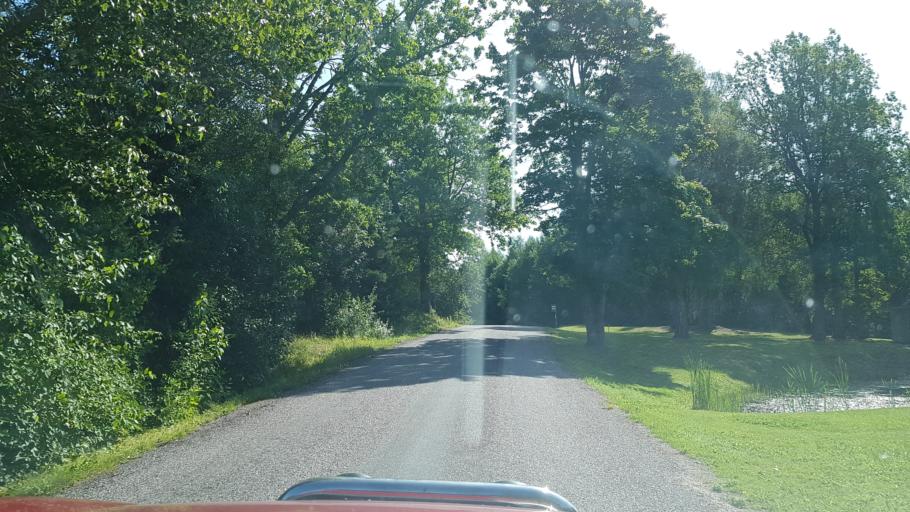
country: EE
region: Vorumaa
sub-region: Voru linn
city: Voru
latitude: 57.7084
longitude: 27.1811
